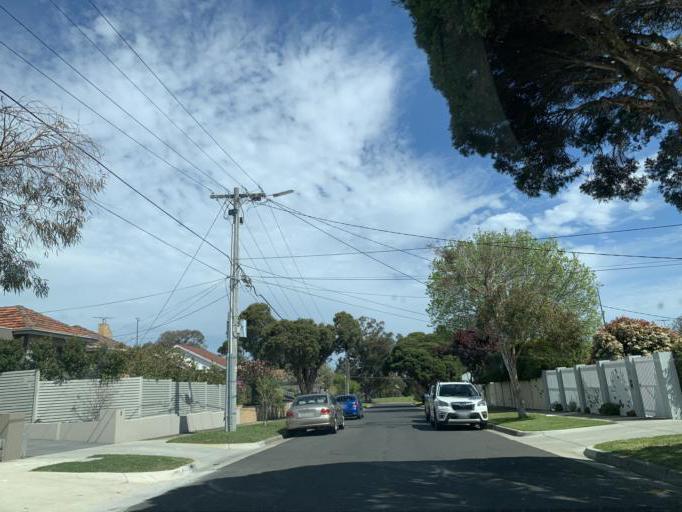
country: AU
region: Victoria
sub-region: Bayside
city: Hampton East
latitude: -37.9442
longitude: 145.0268
